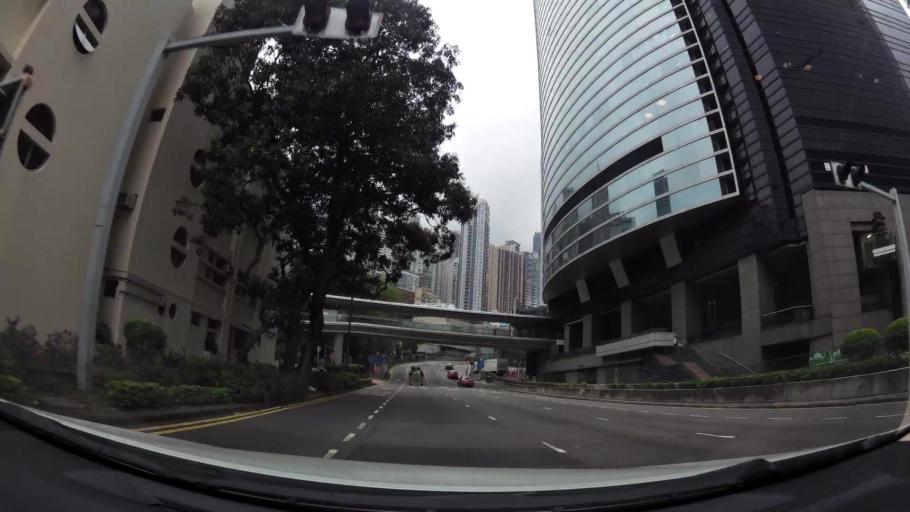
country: HK
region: Central and Western
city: Central
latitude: 22.2785
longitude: 114.1616
